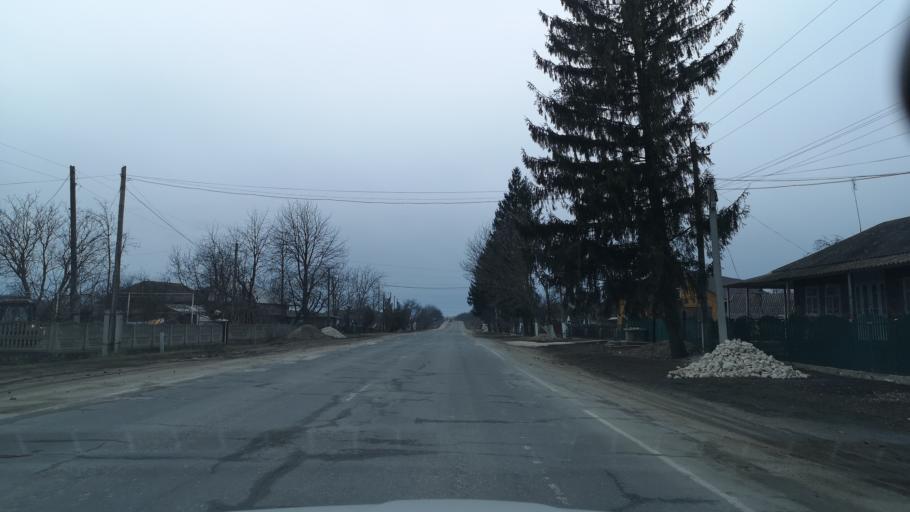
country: MD
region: Briceni
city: Briceni
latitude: 48.3256
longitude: 27.0203
